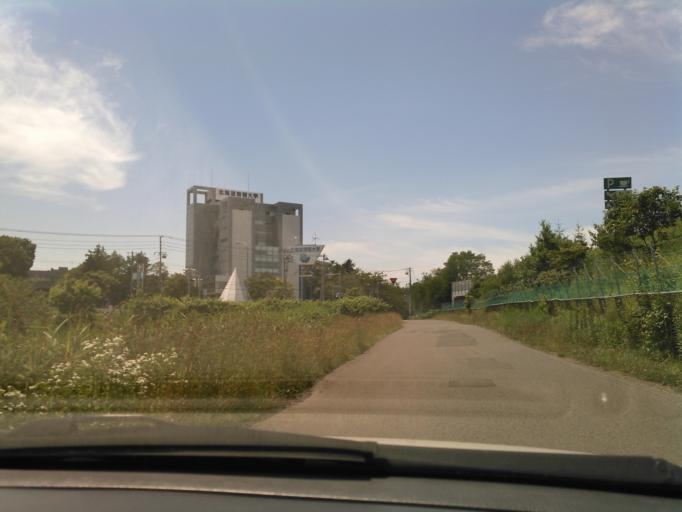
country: JP
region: Hokkaido
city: Ebetsu
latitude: 43.0794
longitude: 141.5406
